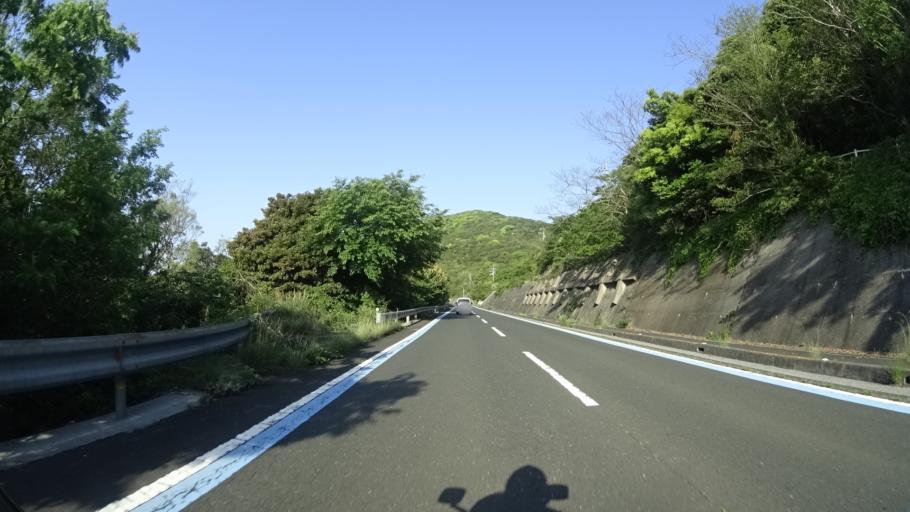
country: JP
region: Ehime
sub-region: Nishiuwa-gun
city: Ikata-cho
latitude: 33.4196
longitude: 132.1863
